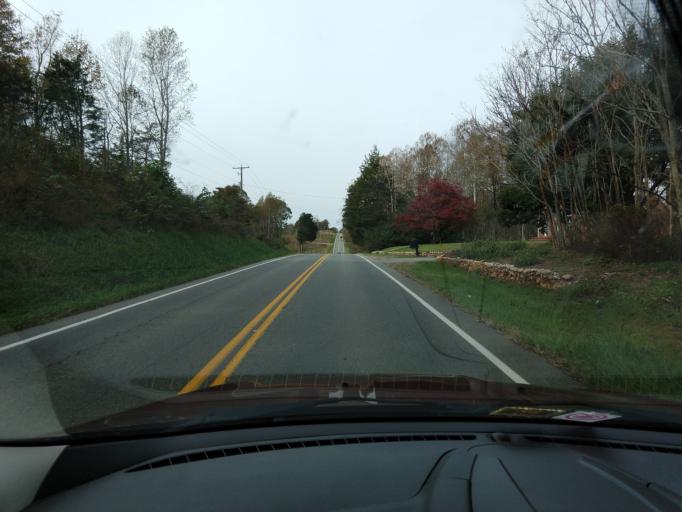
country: US
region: Virginia
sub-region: Franklin County
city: Union Hall
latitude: 36.9888
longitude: -79.6594
